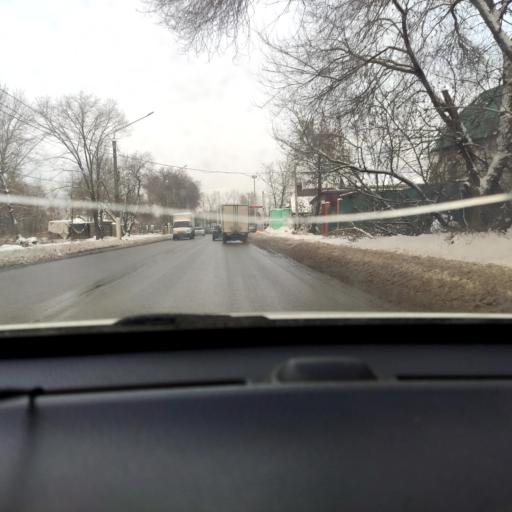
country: RU
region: Voronezj
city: Voronezh
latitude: 51.7302
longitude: 39.2599
